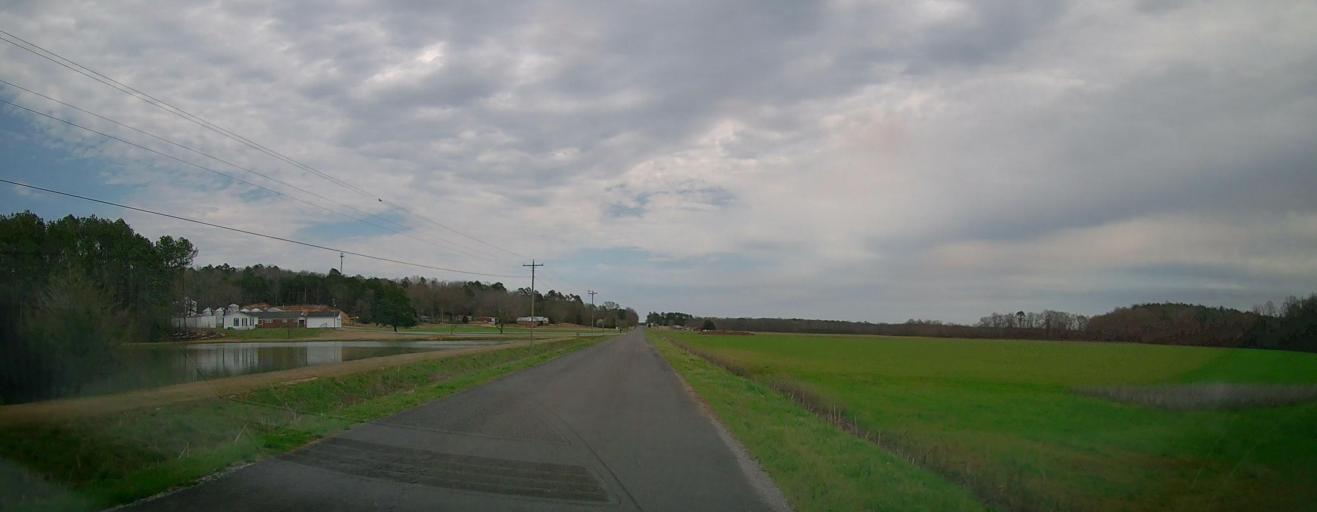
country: US
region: Alabama
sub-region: Marion County
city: Hamilton
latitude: 34.1948
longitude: -88.1586
